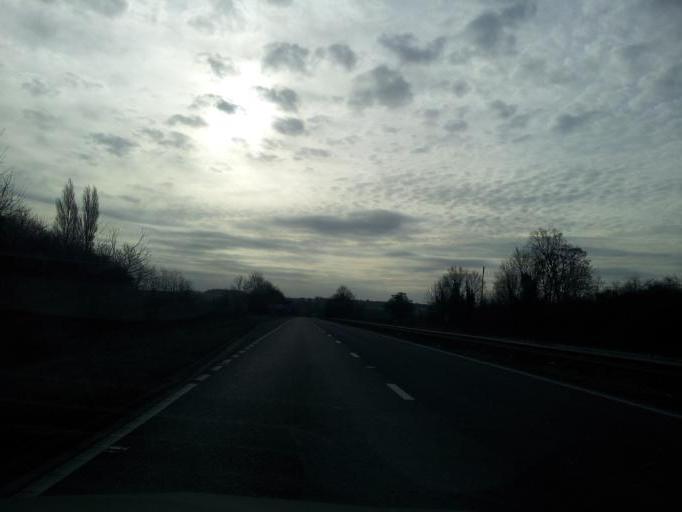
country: GB
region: England
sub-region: District of Rutland
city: Tickencote
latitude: 52.6757
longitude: -0.5346
